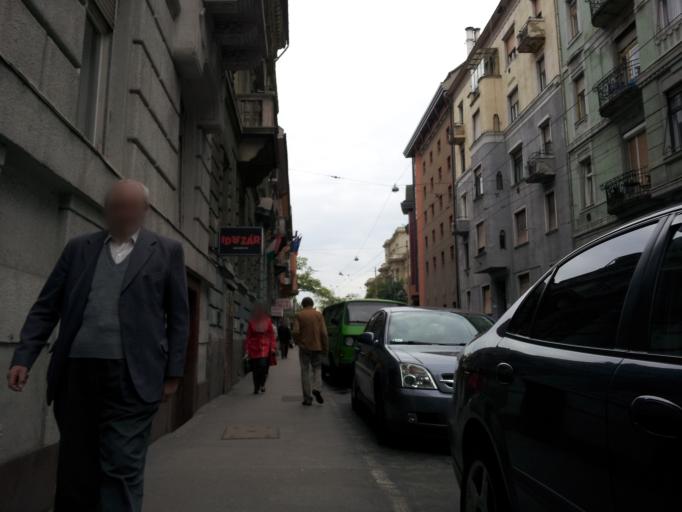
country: HU
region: Budapest
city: Budapest XIII. keruelet
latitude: 47.5164
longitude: 19.0740
